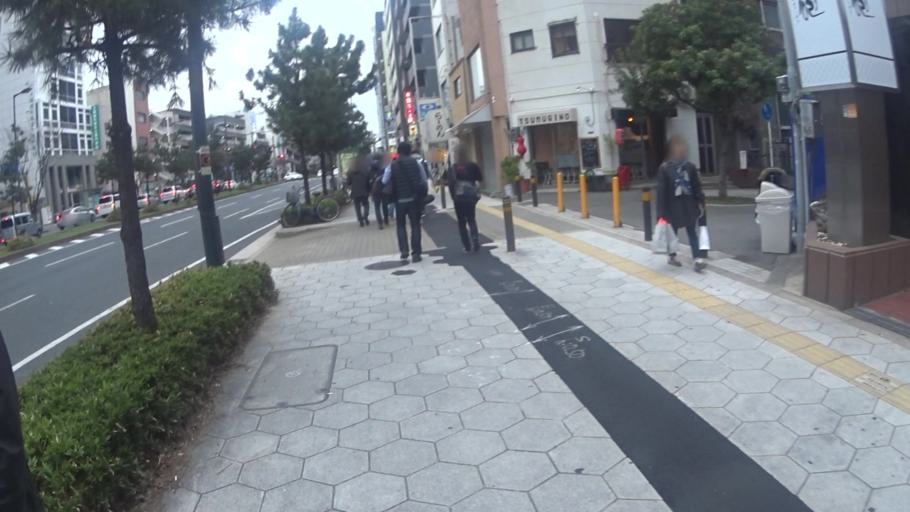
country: JP
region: Osaka
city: Osaka-shi
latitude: 34.6647
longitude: 135.5253
